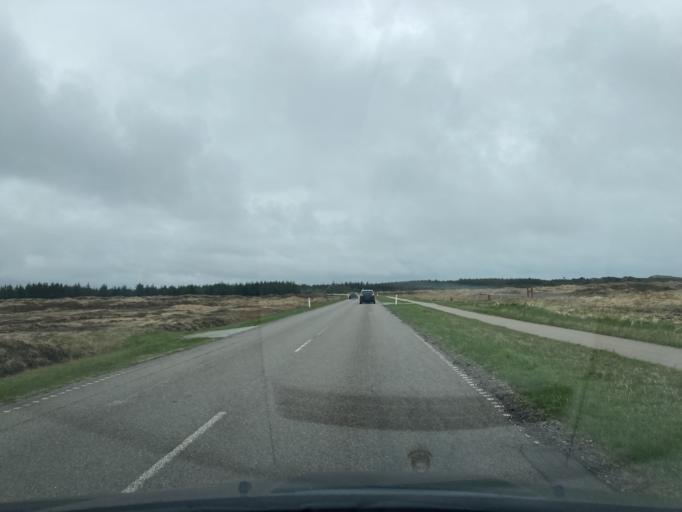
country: DK
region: North Denmark
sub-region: Thisted Kommune
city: Hanstholm
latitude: 56.9867
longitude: 8.4380
